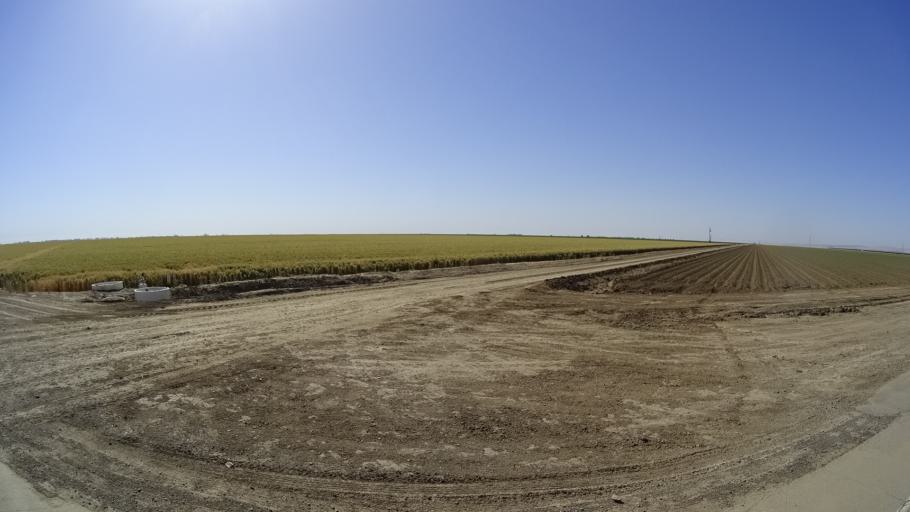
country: US
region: California
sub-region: Kings County
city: Lemoore Station
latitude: 36.1926
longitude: -119.9413
